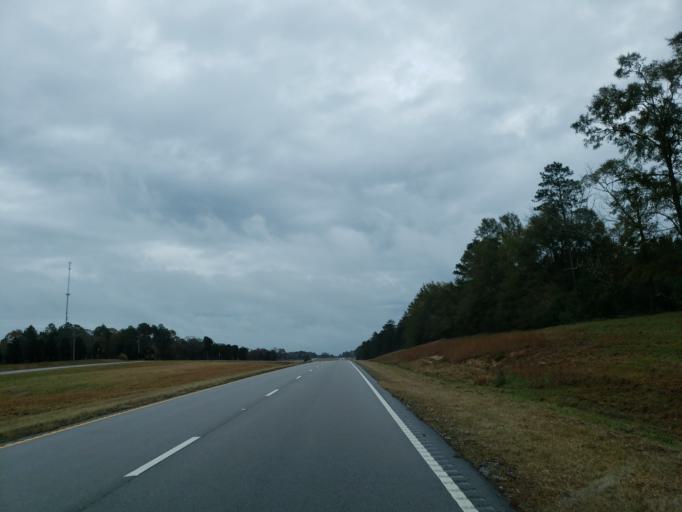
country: US
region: Mississippi
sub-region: Wayne County
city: Waynesboro
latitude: 31.6954
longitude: -88.7444
